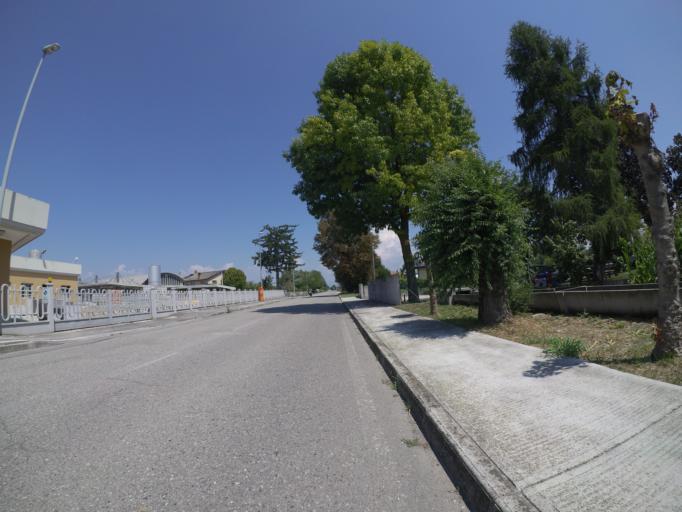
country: IT
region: Friuli Venezia Giulia
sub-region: Provincia di Udine
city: Talmassons
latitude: 45.9258
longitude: 13.1503
